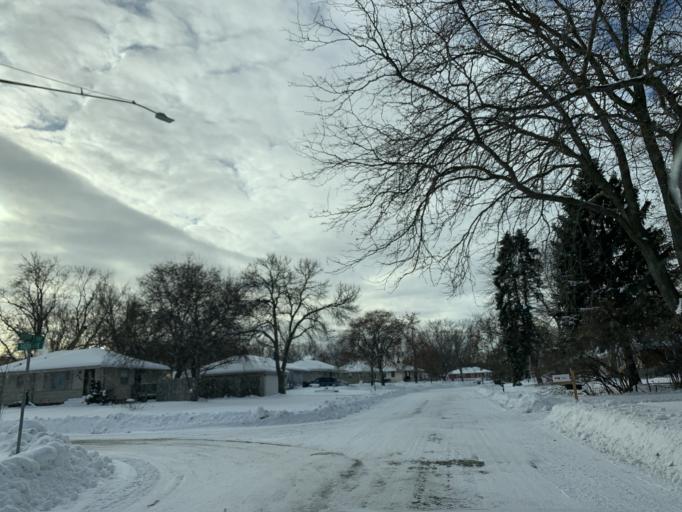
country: US
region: Minnesota
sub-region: Anoka County
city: Coon Rapids
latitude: 45.1707
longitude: -93.2910
